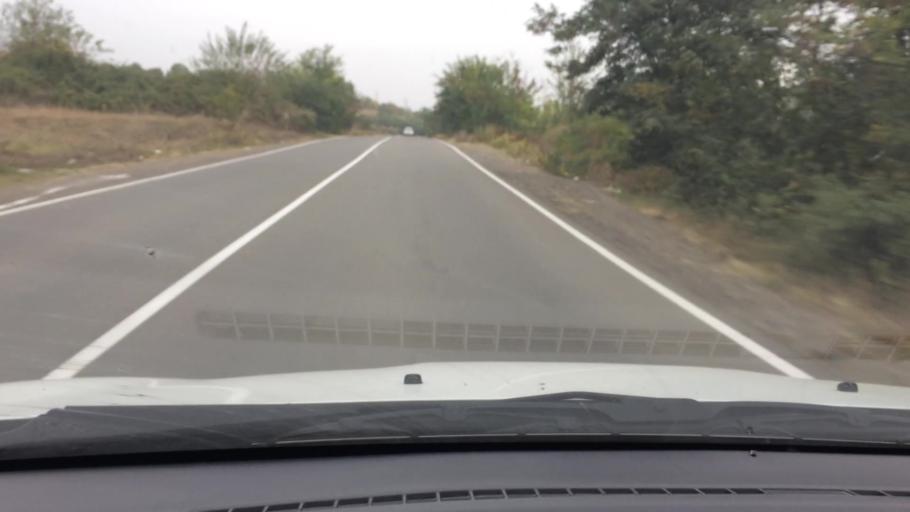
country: AM
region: Tavush
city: Bagratashen
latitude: 41.2713
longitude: 44.7907
